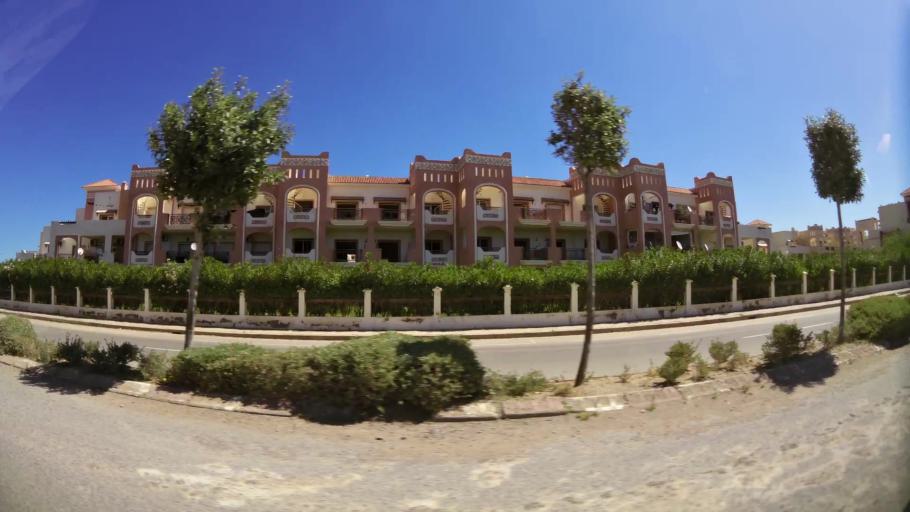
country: MA
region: Oriental
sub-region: Berkane-Taourirt
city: Madagh
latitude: 35.1042
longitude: -2.3148
